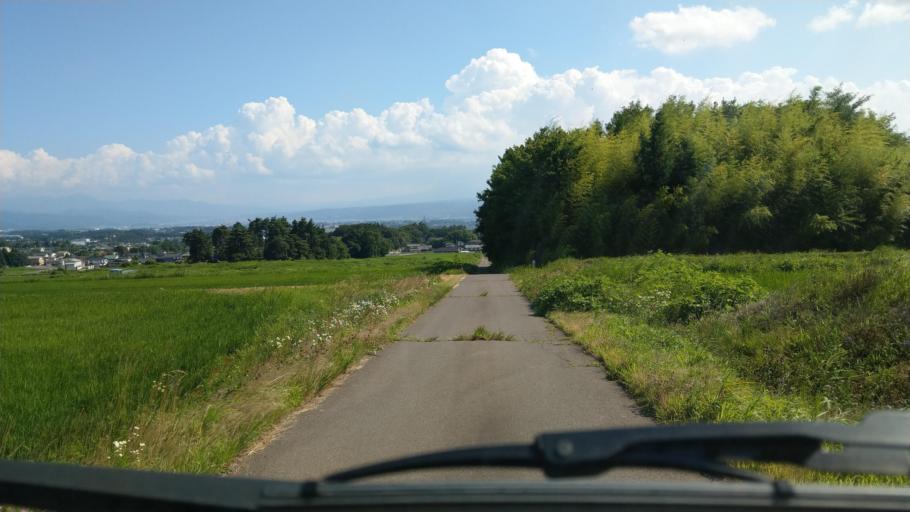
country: JP
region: Nagano
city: Komoro
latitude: 36.3272
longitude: 138.4504
